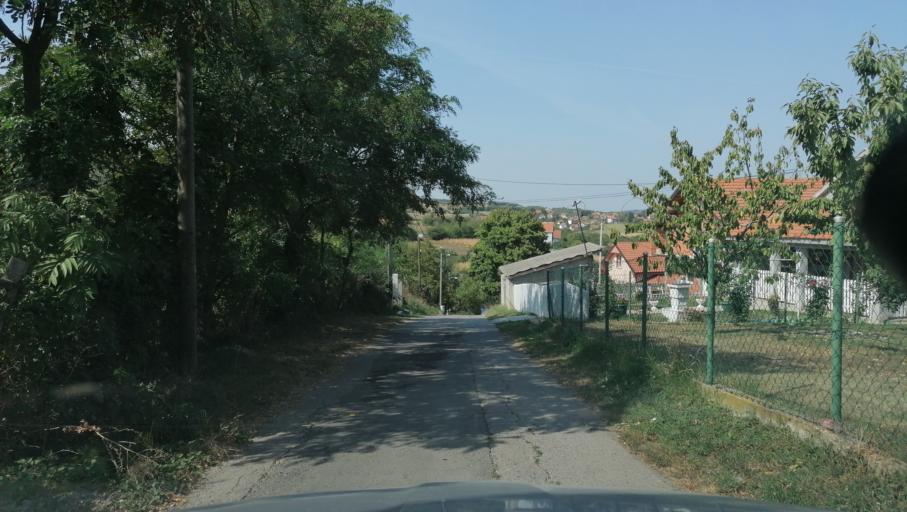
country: RS
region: Central Serbia
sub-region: Belgrade
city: Zvezdara
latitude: 44.6906
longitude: 20.5516
